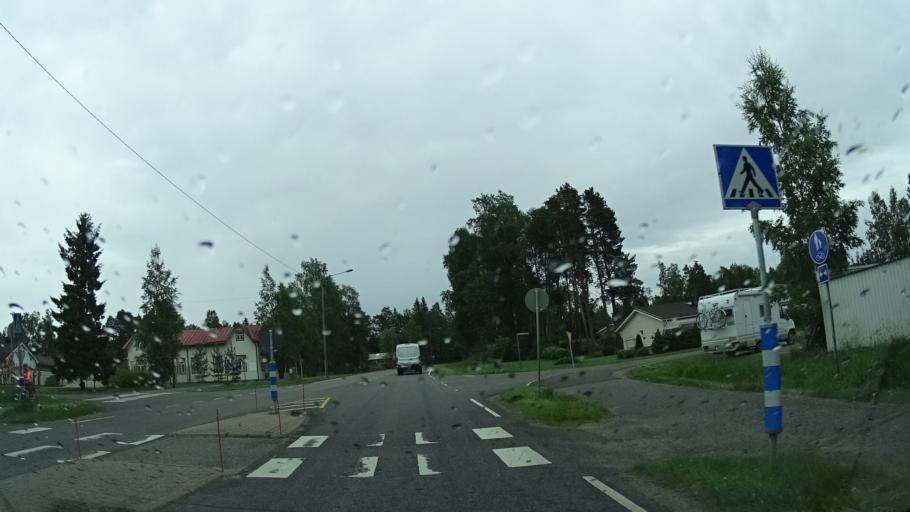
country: FI
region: Varsinais-Suomi
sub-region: Loimaa
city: Aura
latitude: 60.6464
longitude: 22.5965
